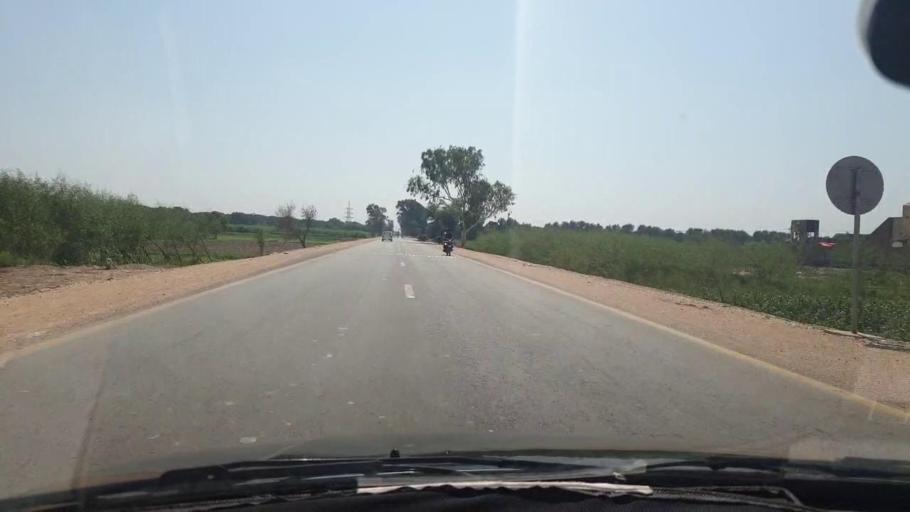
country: PK
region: Sindh
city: Chambar
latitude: 25.3745
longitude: 68.7797
